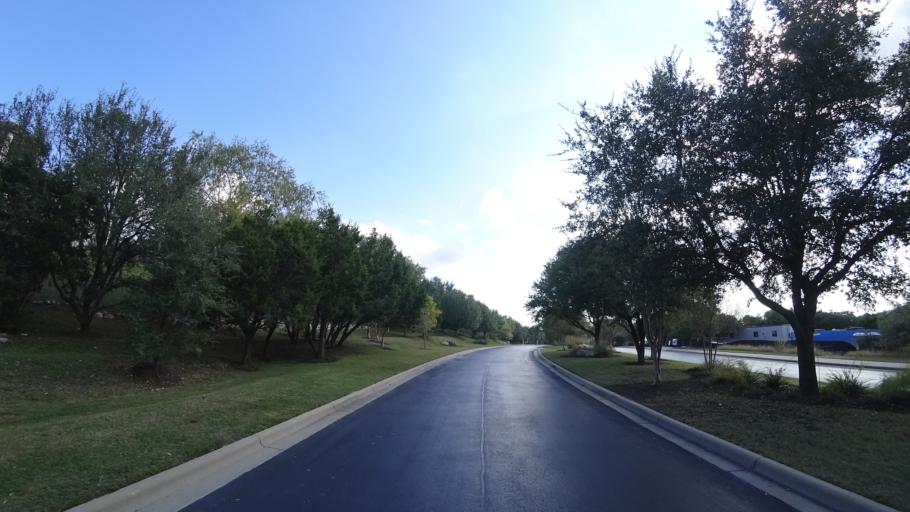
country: US
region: Texas
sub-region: Travis County
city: Barton Creek
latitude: 30.2906
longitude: -97.8659
